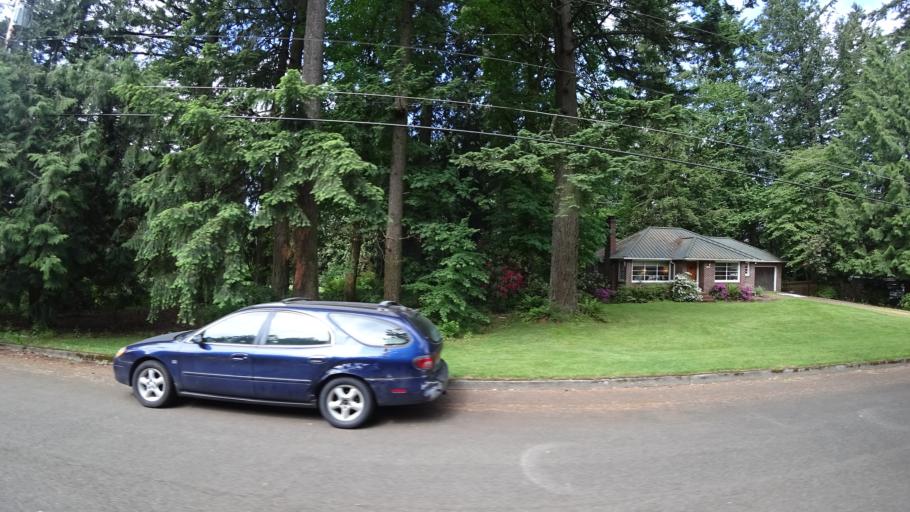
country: US
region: Oregon
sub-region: Washington County
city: Metzger
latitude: 45.4524
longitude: -122.7300
